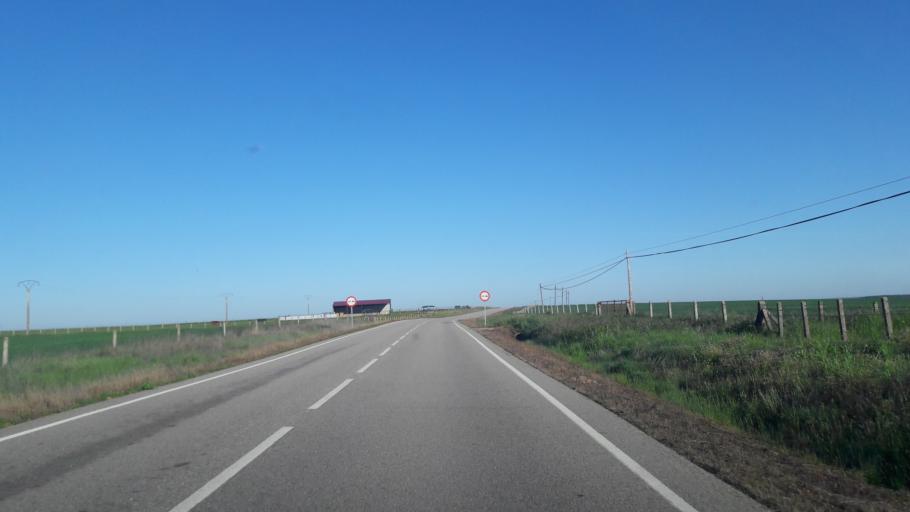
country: ES
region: Castille and Leon
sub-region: Provincia de Salamanca
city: La Fuente de San Esteban
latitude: 40.8059
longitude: -6.2682
